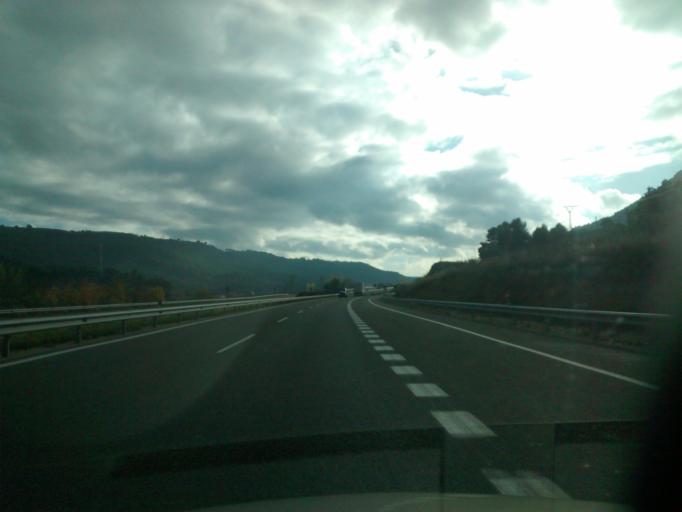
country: ES
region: Castille-La Mancha
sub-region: Provincia de Guadalajara
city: Tortola de Henares
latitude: 40.6905
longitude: -3.0870
